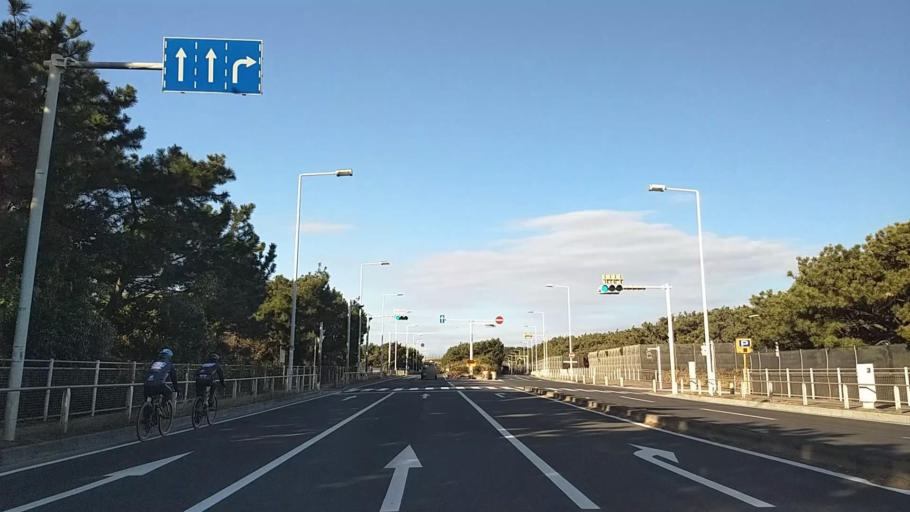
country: JP
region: Kanagawa
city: Fujisawa
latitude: 35.3192
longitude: 139.4514
